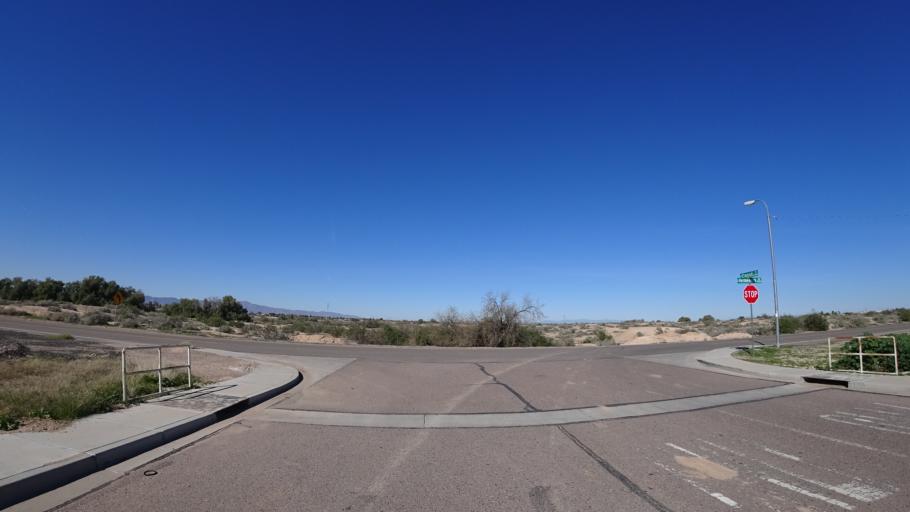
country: US
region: Arizona
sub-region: Maricopa County
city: Avondale
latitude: 33.4136
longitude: -112.3350
